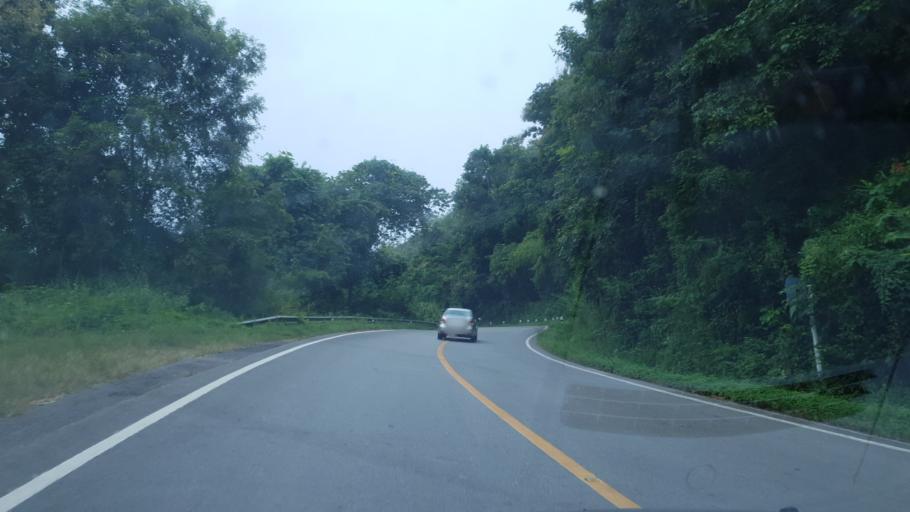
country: TH
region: Mae Hong Son
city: Khun Yuam
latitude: 18.7232
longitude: 97.9079
